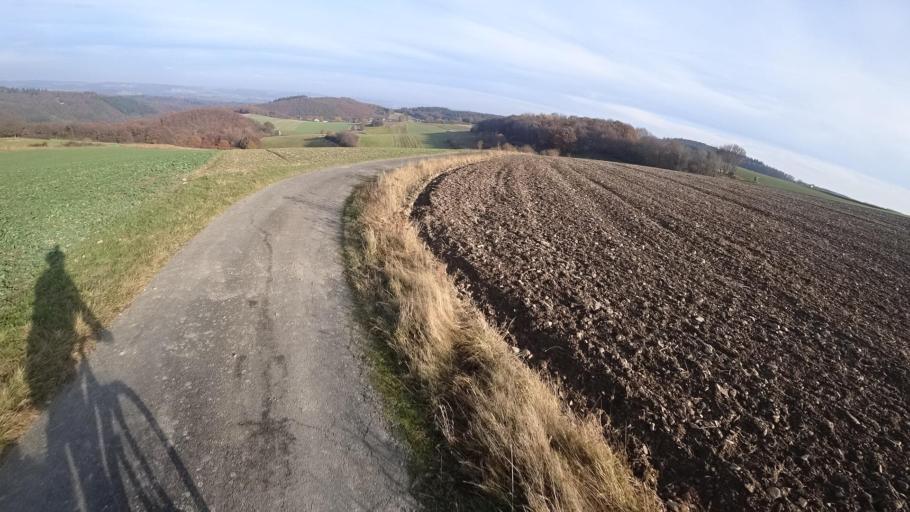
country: DE
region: Rheinland-Pfalz
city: Utzenhain
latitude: 50.1287
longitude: 7.6252
